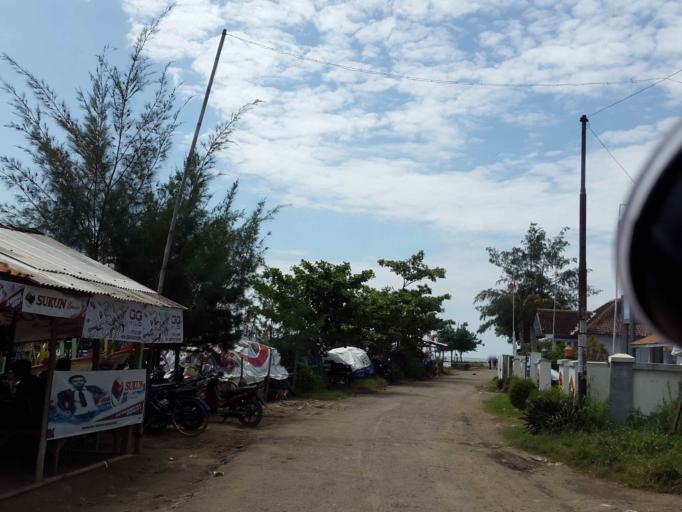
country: ID
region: Central Java
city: Pemalang
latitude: -6.8635
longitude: 109.3681
